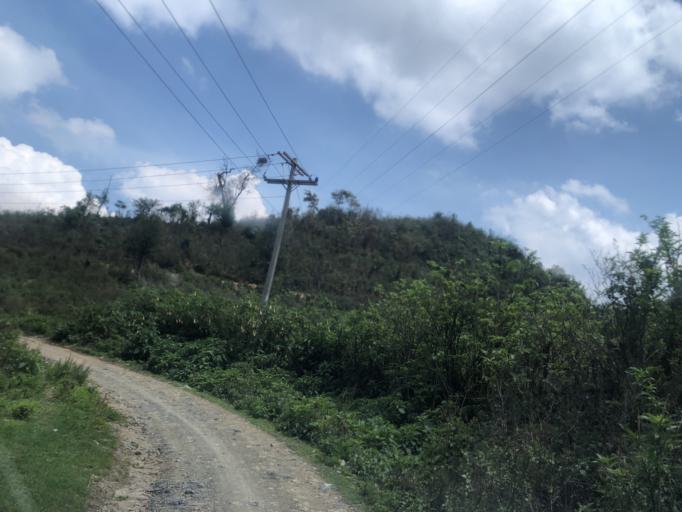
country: LA
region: Phongsali
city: Phongsali
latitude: 21.3909
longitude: 102.1924
